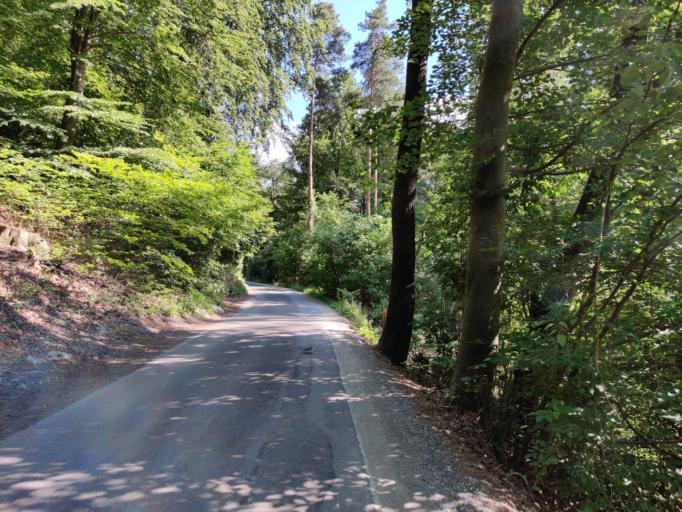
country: AT
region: Styria
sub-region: Graz Stadt
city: Wetzelsdorf
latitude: 47.0362
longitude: 15.3671
